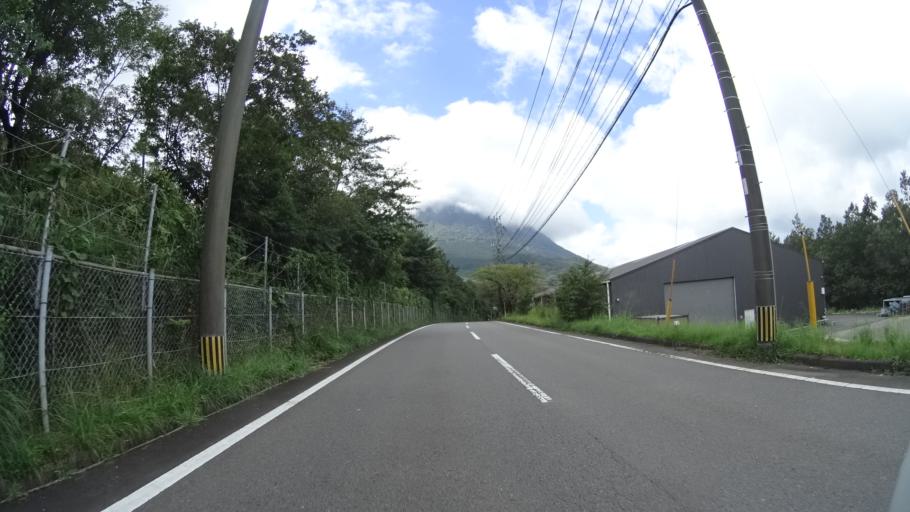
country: JP
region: Oita
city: Beppu
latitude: 33.3074
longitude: 131.4050
